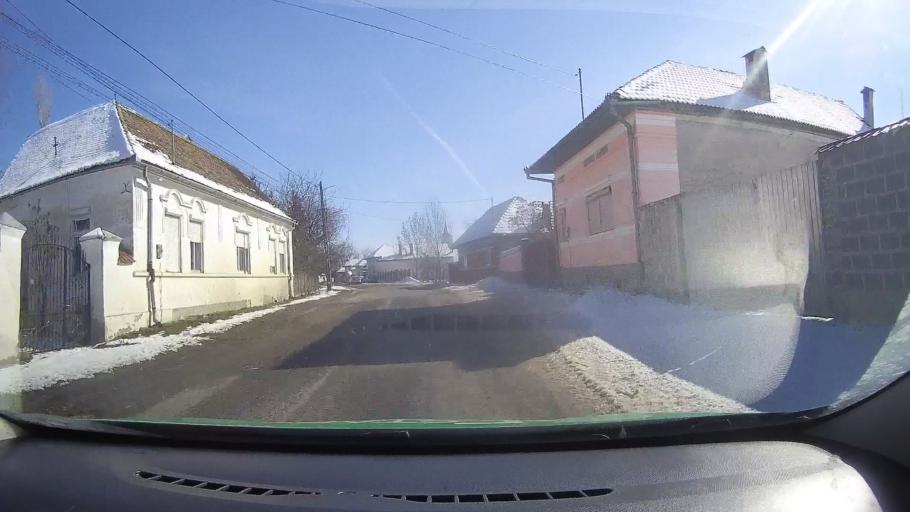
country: RO
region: Brasov
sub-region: Comuna Recea
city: Recea
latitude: 45.7332
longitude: 24.9365
